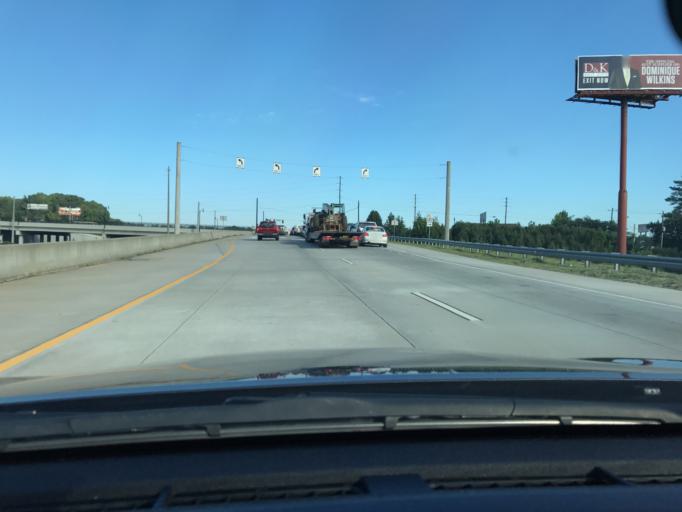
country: US
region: Georgia
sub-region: DeKalb County
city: Scottdale
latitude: 33.7771
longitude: -84.2388
